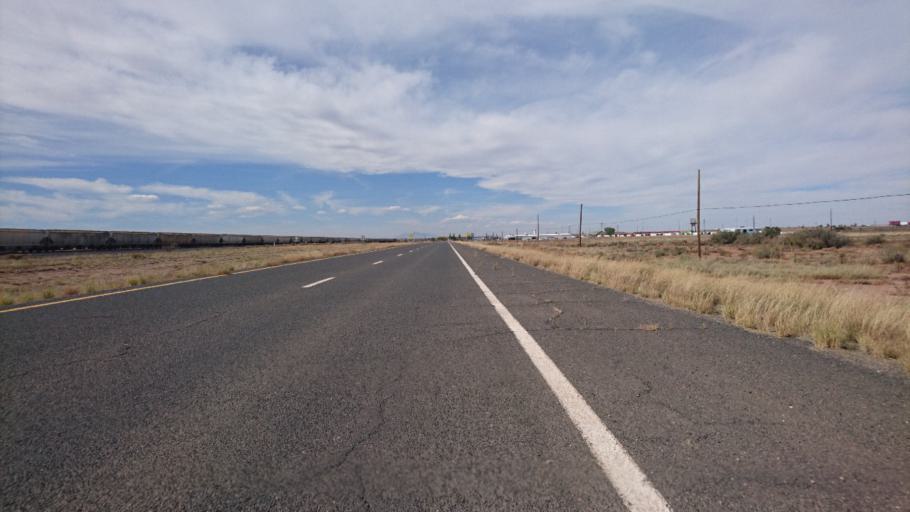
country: US
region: Arizona
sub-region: Navajo County
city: Winslow
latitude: 35.0107
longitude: -110.6679
